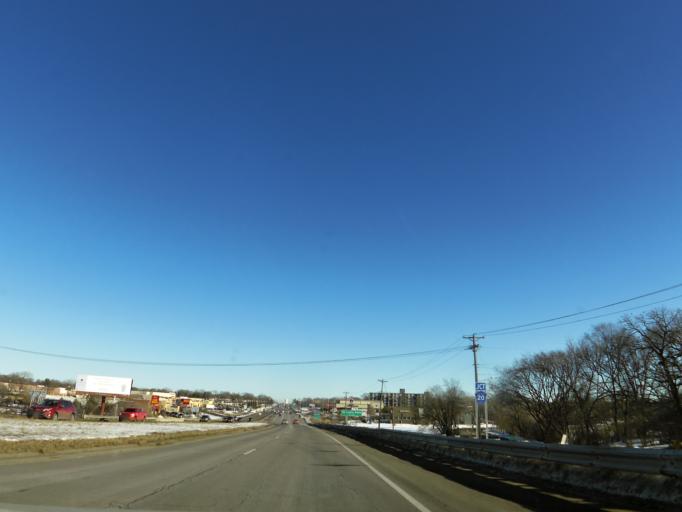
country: US
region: Minnesota
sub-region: Hennepin County
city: Saint Louis Park
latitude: 44.9348
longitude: -93.3915
